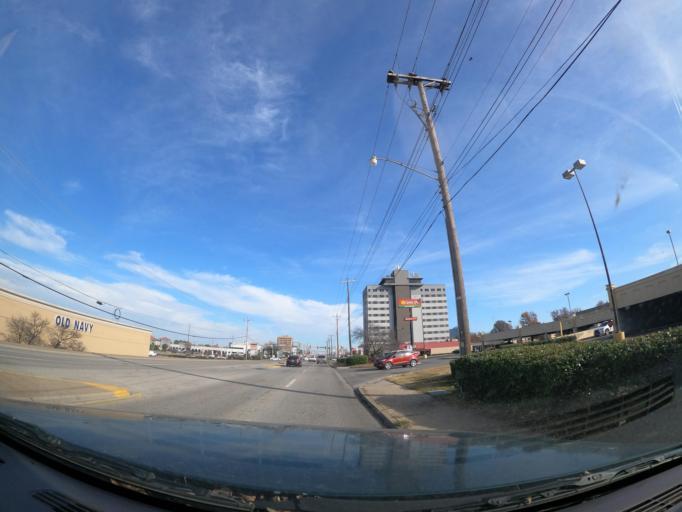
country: US
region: Oklahoma
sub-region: Tulsa County
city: Tulsa
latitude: 36.1044
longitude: -95.9189
